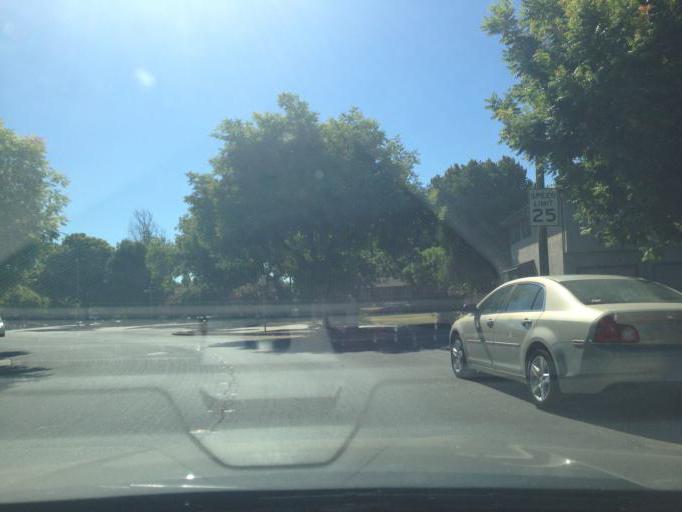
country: US
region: California
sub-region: Santa Clara County
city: Seven Trees
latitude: 37.2451
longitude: -121.8645
